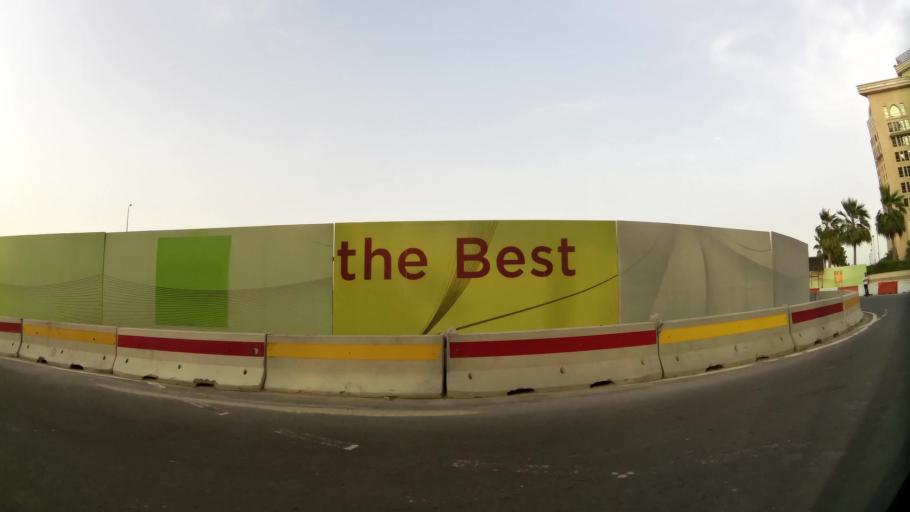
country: QA
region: Baladiyat ad Dawhah
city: Doha
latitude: 25.3510
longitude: 51.5285
